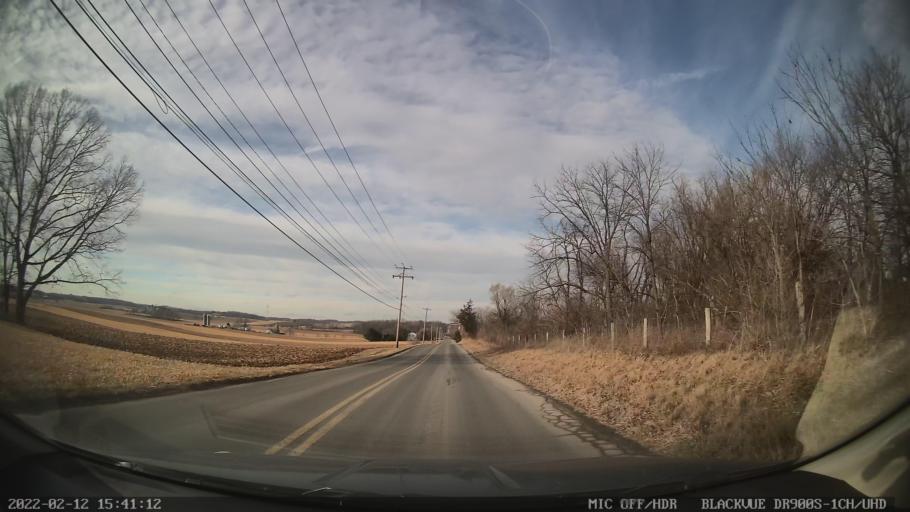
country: US
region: Pennsylvania
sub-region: Berks County
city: Topton
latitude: 40.5196
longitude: -75.7313
